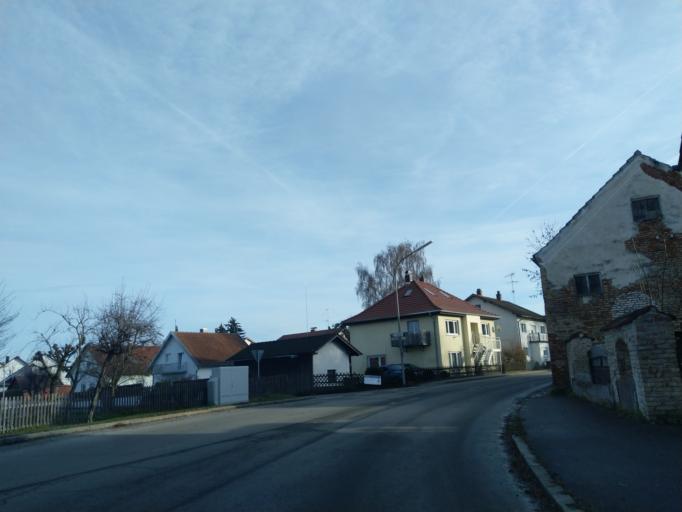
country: DE
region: Bavaria
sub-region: Lower Bavaria
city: Wallerfing
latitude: 48.6859
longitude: 12.8793
